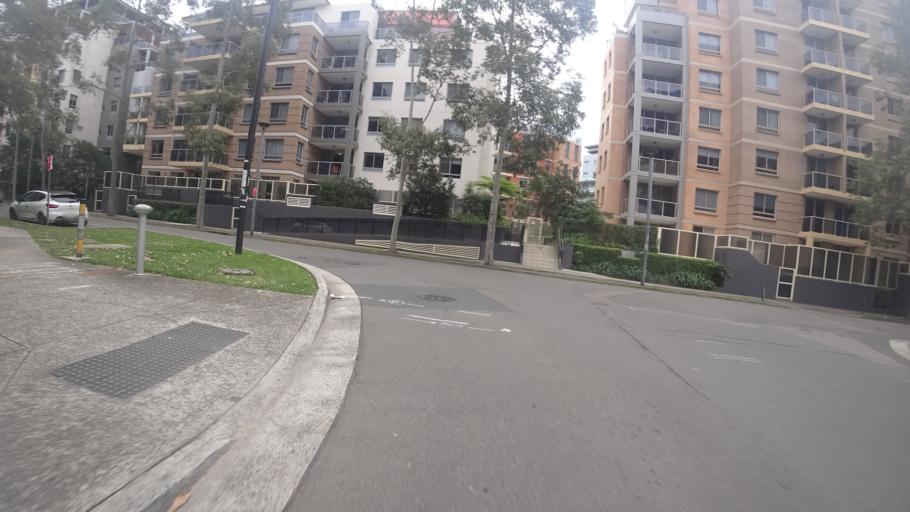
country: AU
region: New South Wales
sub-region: Rockdale
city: Arncliffe
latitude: -33.9299
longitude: 151.1503
